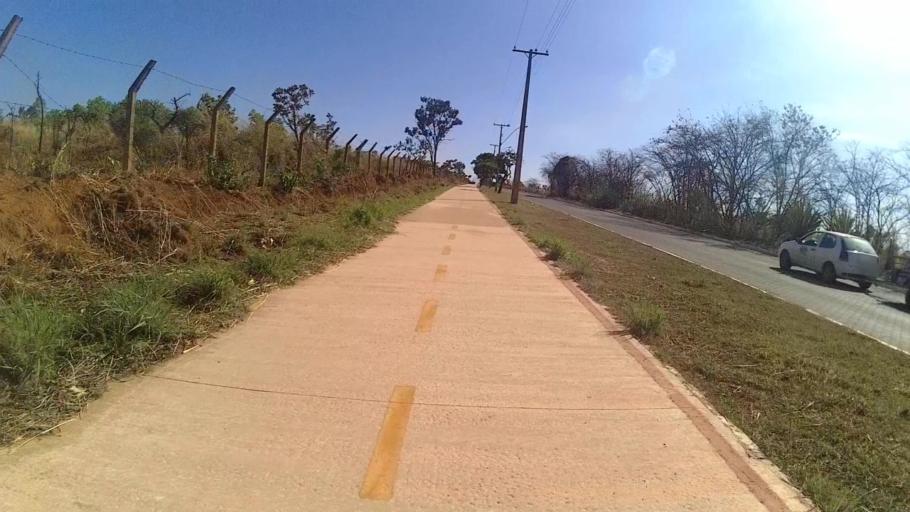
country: BR
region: Federal District
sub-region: Brasilia
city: Brasilia
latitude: -15.6522
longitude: -47.8937
